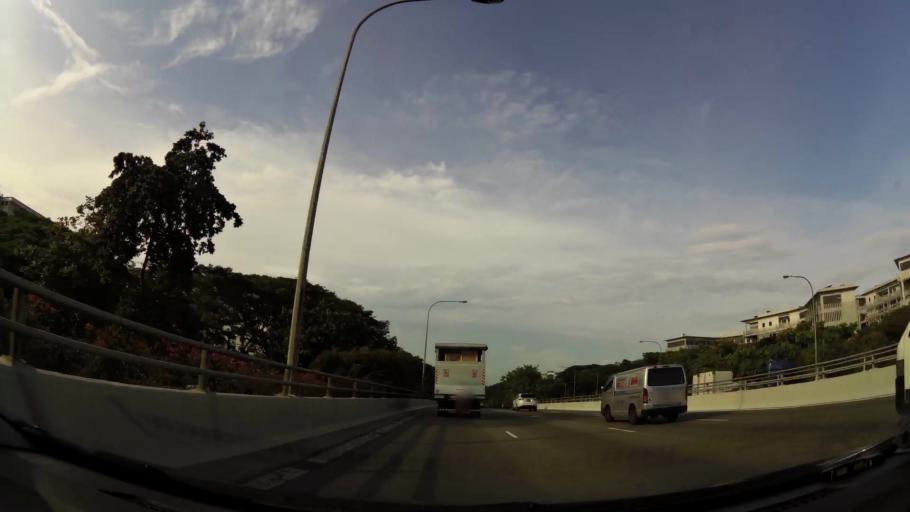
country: MY
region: Johor
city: Johor Bahru
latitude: 1.3458
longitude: 103.6904
